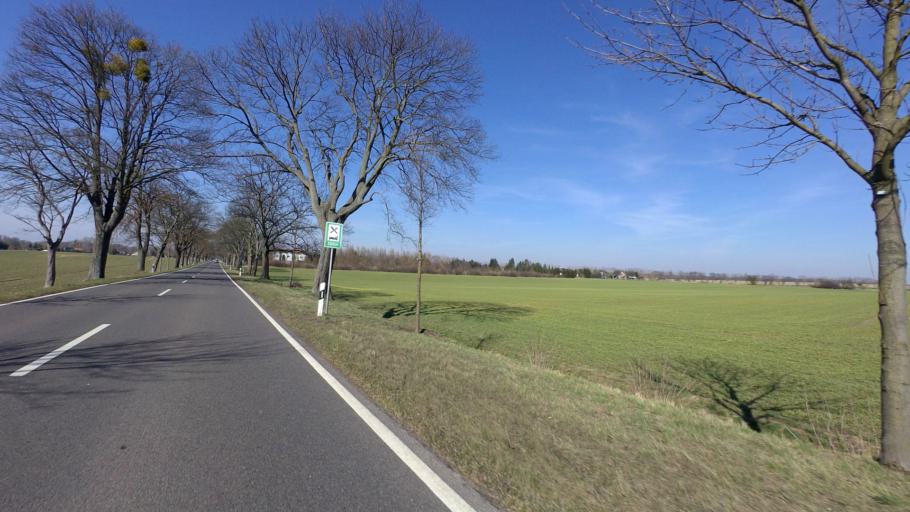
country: DE
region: Brandenburg
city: Eberswalde
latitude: 52.7661
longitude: 13.8394
